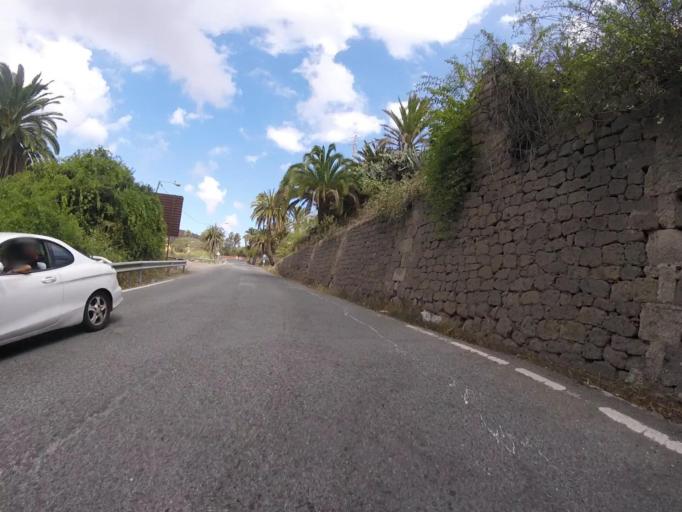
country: ES
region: Canary Islands
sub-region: Provincia de Las Palmas
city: Santa Brigida
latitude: 28.0574
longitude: -15.4652
